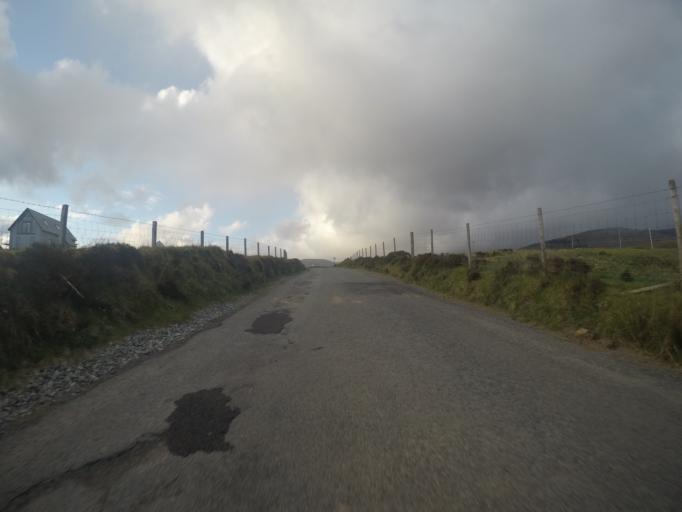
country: GB
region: Scotland
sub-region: Highland
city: Isle of Skye
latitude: 57.4565
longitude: -6.2975
